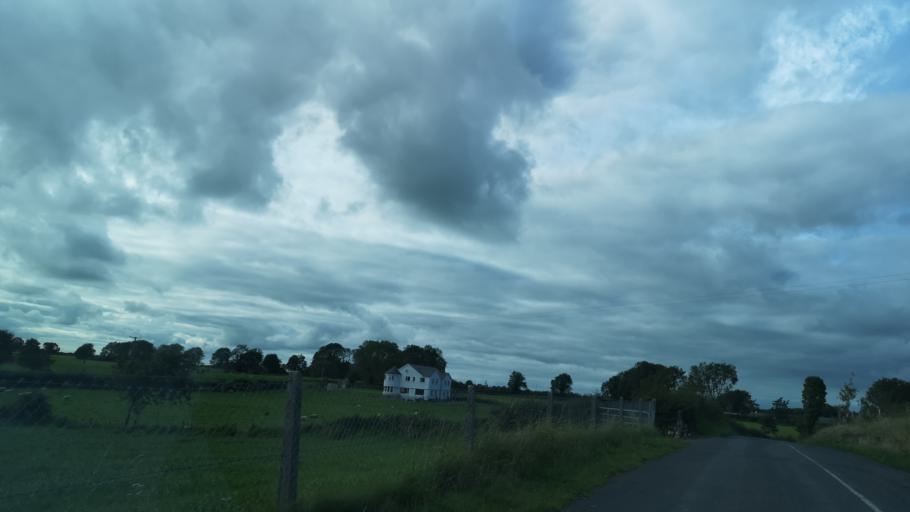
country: IE
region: Connaught
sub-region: County Galway
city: Ballinasloe
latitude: 53.2956
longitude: -8.1030
